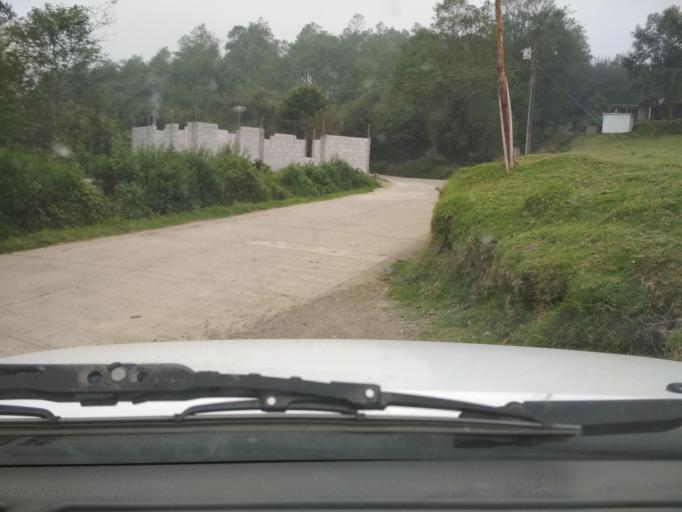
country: MX
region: Veracruz
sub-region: La Perla
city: Chilapa
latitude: 18.9962
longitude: -97.1473
